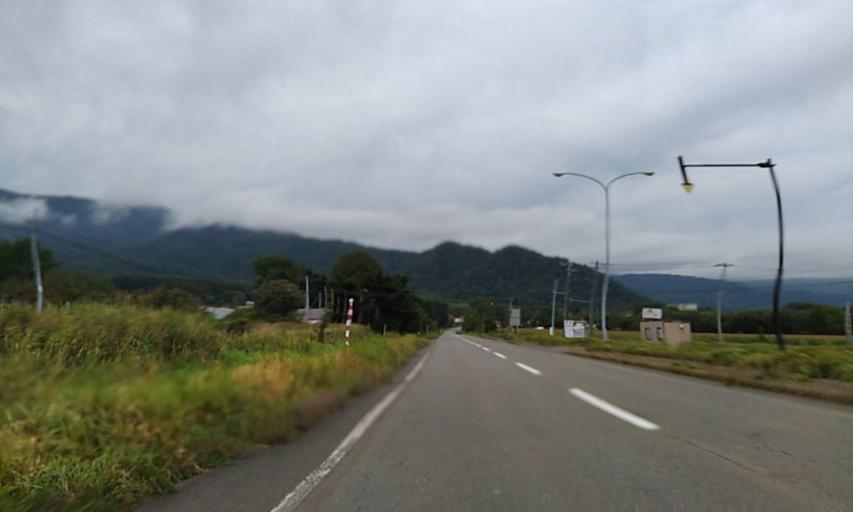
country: JP
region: Hokkaido
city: Bihoro
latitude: 43.5797
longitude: 144.2808
